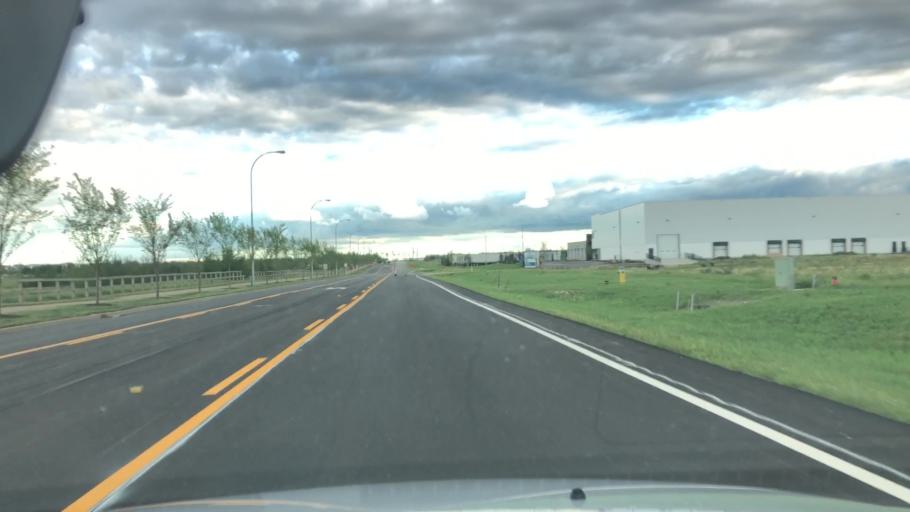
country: CA
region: Alberta
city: St. Albert
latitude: 53.6194
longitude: -113.5698
